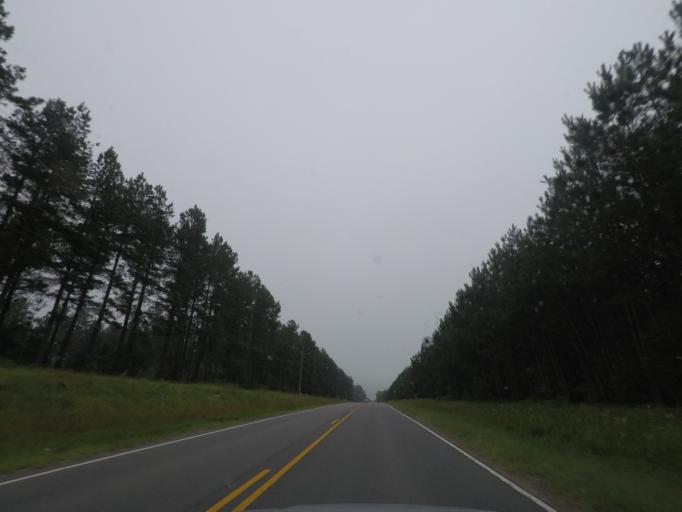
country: US
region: Virginia
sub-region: Buckingham County
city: Buckingham
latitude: 37.5990
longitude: -78.3950
